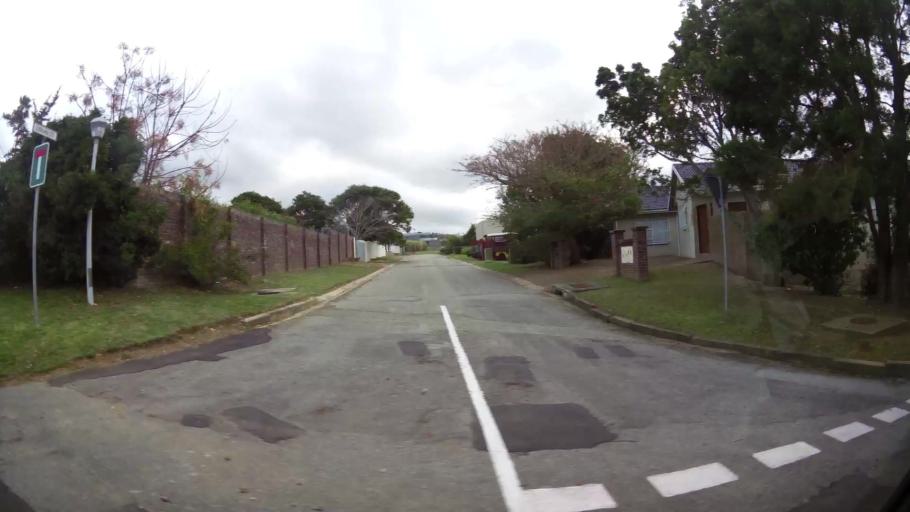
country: ZA
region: Western Cape
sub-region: Eden District Municipality
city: Plettenberg Bay
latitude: -34.0532
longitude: 23.3676
